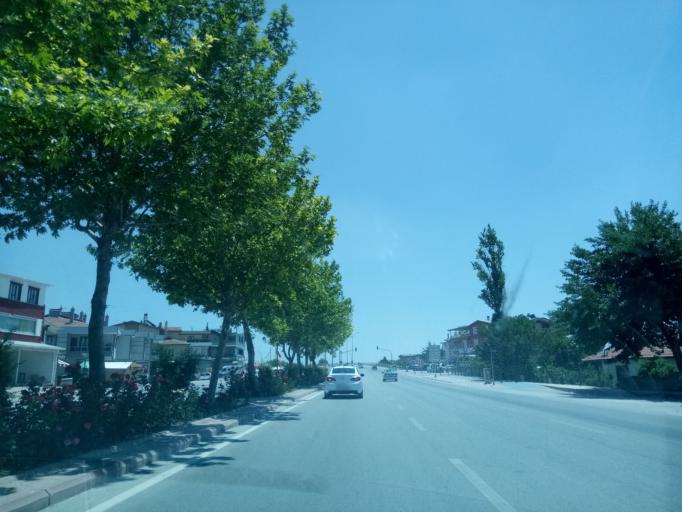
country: TR
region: Konya
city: Meram
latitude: 37.8298
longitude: 32.4886
